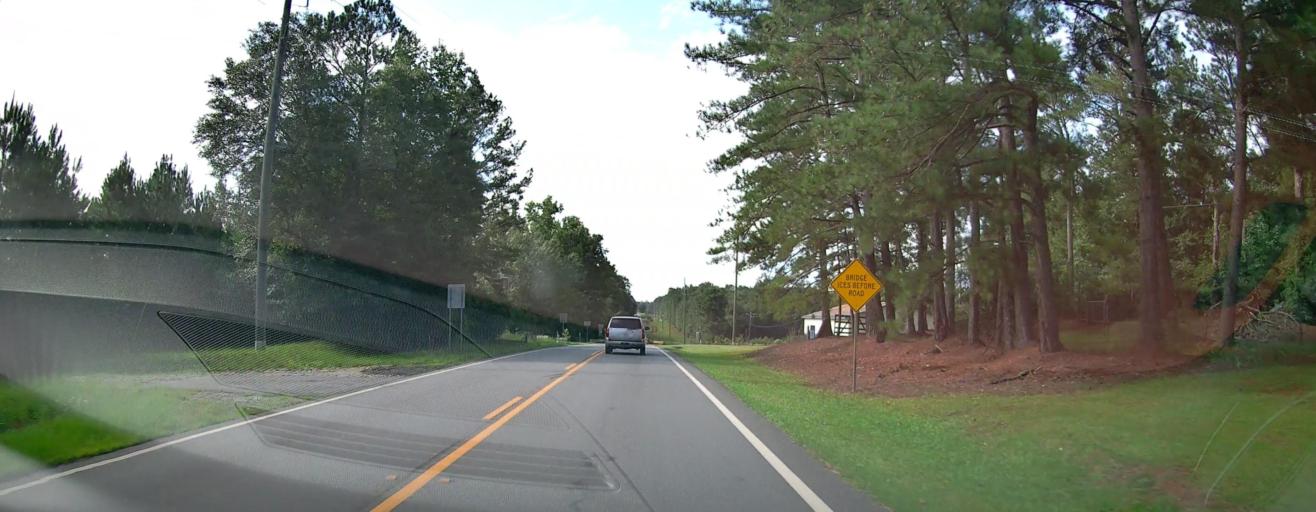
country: US
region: Georgia
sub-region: Upson County
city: Hannahs Mill
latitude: 32.9815
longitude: -84.4984
